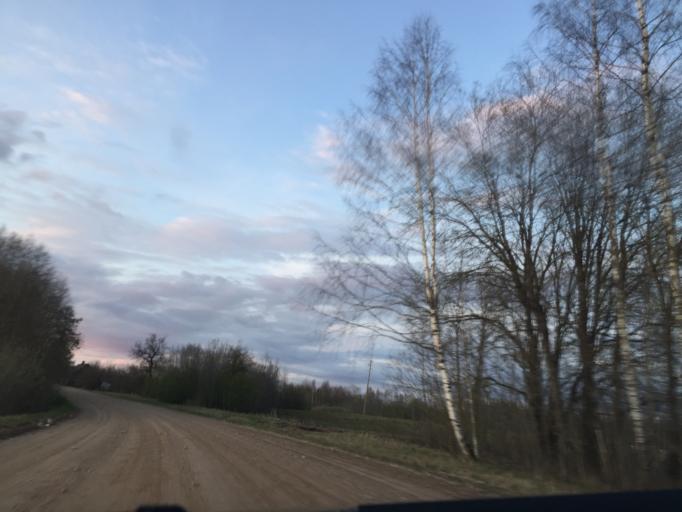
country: LV
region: Aluksnes Rajons
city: Aluksne
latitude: 57.3562
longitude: 26.9864
